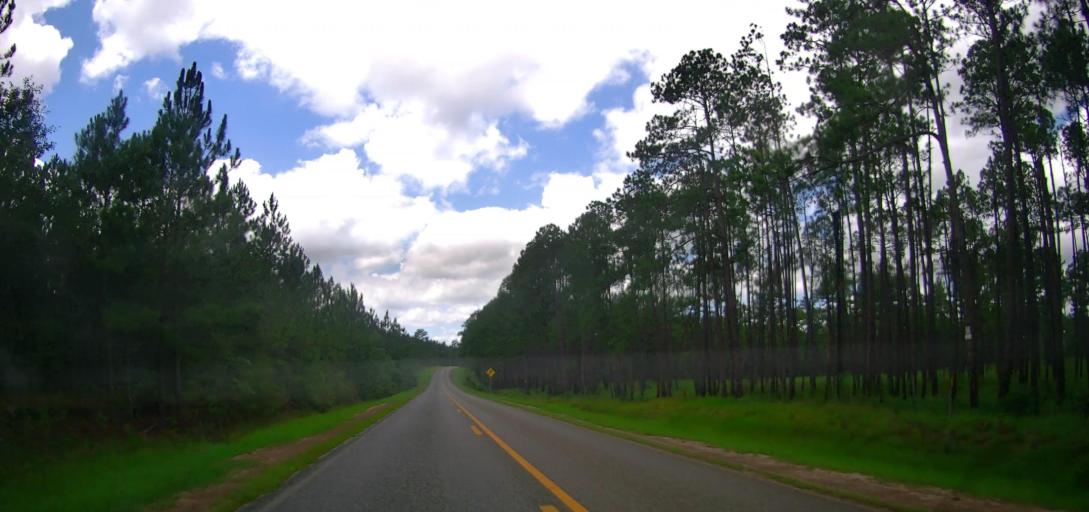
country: US
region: Georgia
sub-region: Turner County
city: Ashburn
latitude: 31.6980
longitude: -83.4912
